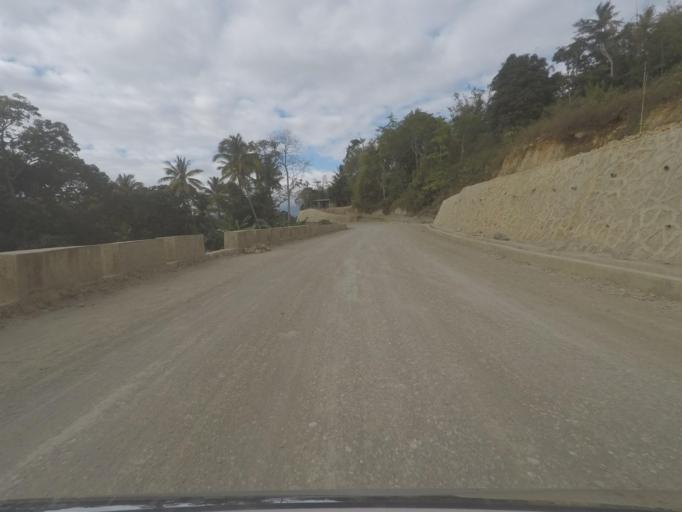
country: TL
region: Baucau
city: Venilale
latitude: -8.6144
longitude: 126.3828
